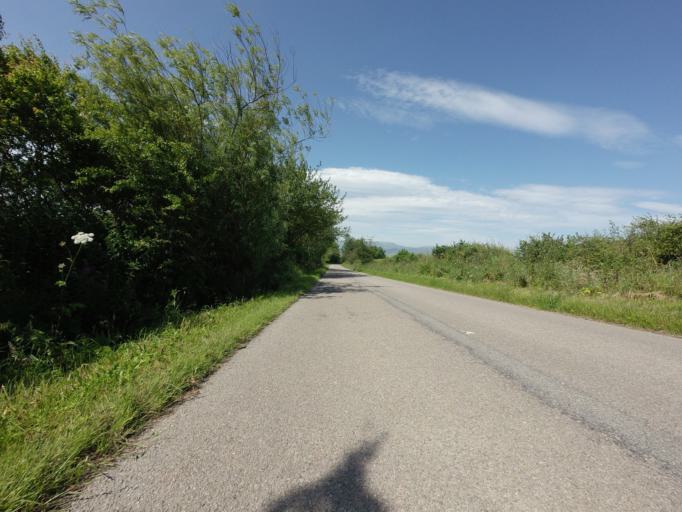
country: GB
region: Scotland
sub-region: Highland
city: Conon Bridge
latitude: 57.5530
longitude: -4.4053
